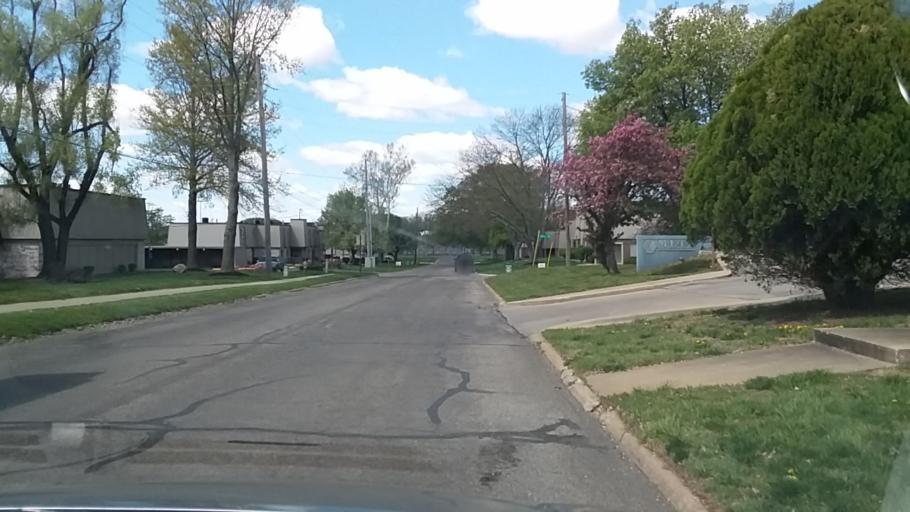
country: US
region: Kansas
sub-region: Douglas County
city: Lawrence
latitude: 38.9387
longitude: -95.2628
